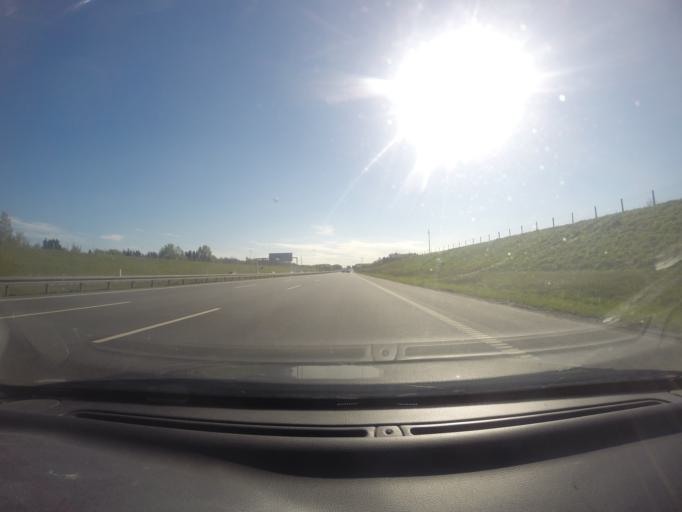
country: DK
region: Capital Region
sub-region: Ballerup Kommune
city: Ballerup
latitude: 55.6973
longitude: 12.3620
